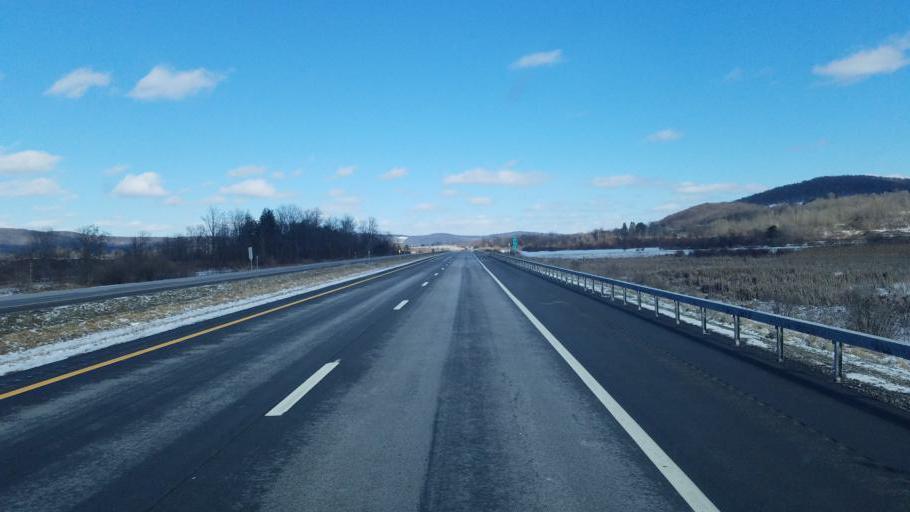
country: US
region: New York
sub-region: Cattaraugus County
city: Allegany
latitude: 42.0894
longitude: -78.5646
